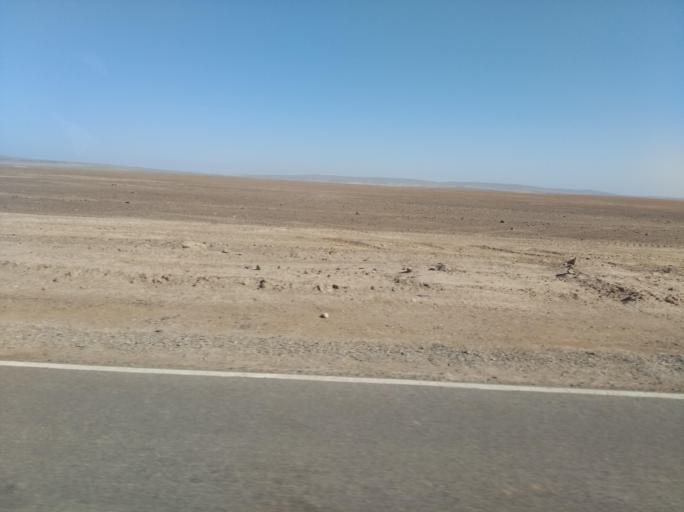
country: CL
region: Atacama
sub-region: Provincia de Copiapo
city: Copiapo
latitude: -27.3166
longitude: -70.8480
